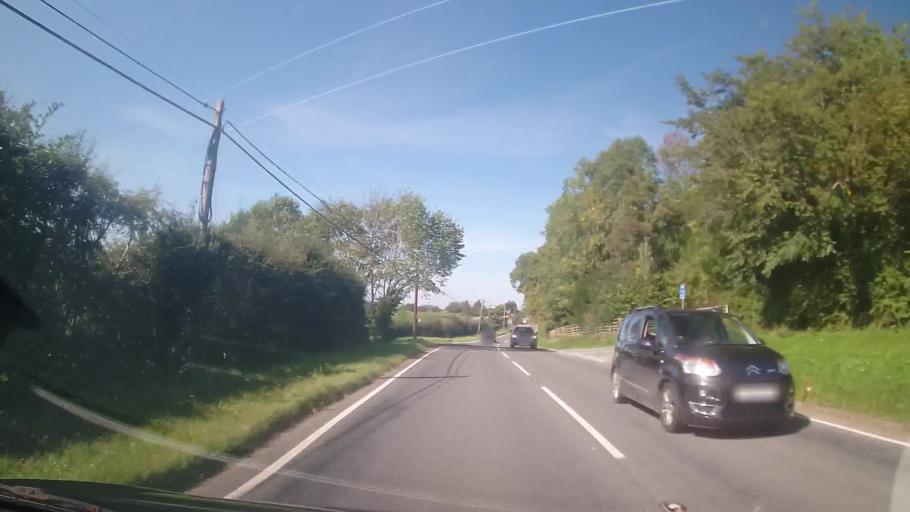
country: GB
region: England
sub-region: Shropshire
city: Mainstone
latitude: 52.5338
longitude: -3.0560
